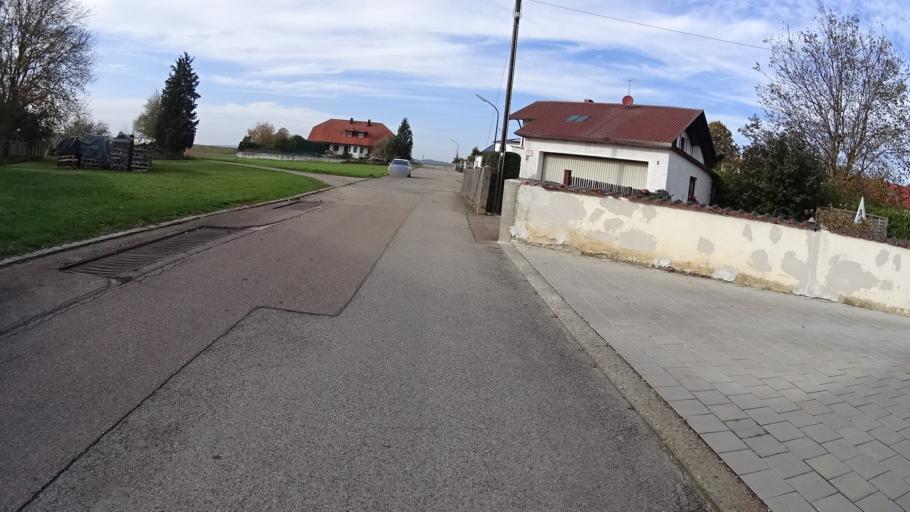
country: DE
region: Bavaria
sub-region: Upper Bavaria
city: Eitensheim
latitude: 48.8190
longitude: 11.3149
